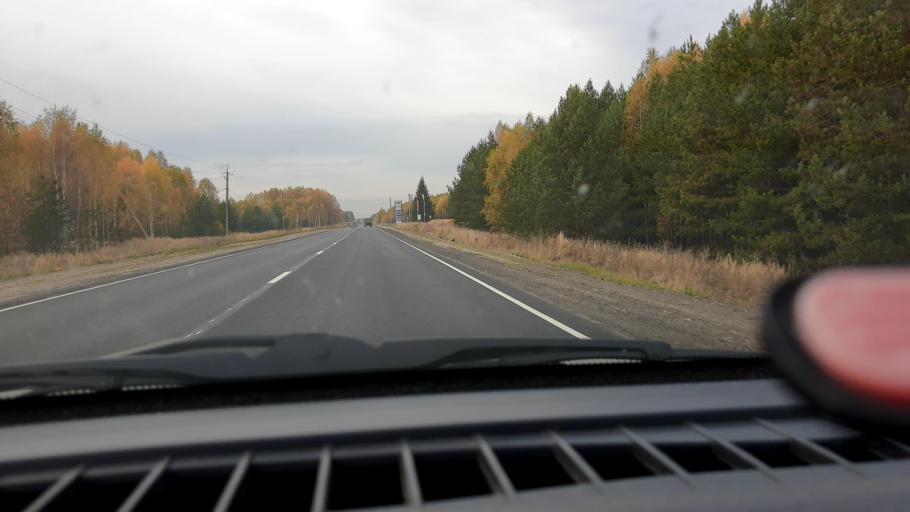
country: RU
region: Nizjnij Novgorod
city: Novaya Balakhna
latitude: 56.5994
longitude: 43.6366
